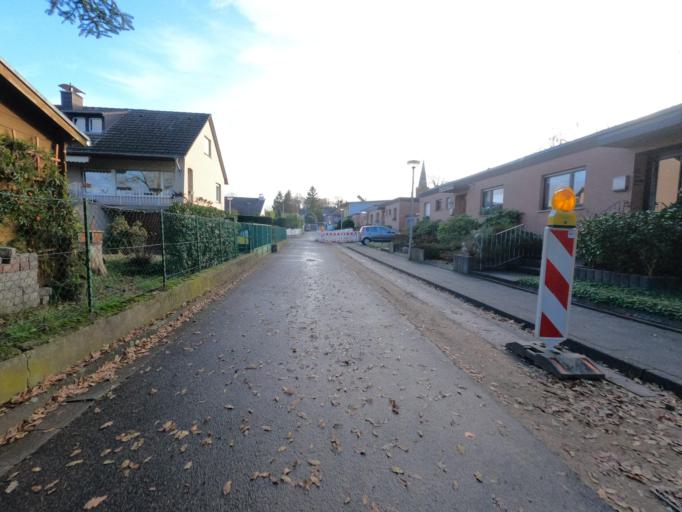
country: DE
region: North Rhine-Westphalia
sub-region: Regierungsbezirk Koln
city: Heinsberg
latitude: 51.0613
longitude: 6.0888
